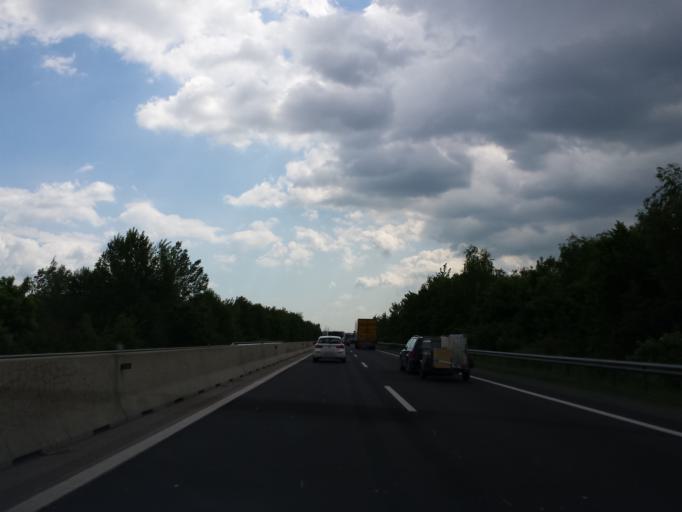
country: AT
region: Burgenland
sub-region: Politischer Bezirk Neusiedl am See
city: Bruckneudorf
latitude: 48.0405
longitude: 16.7968
